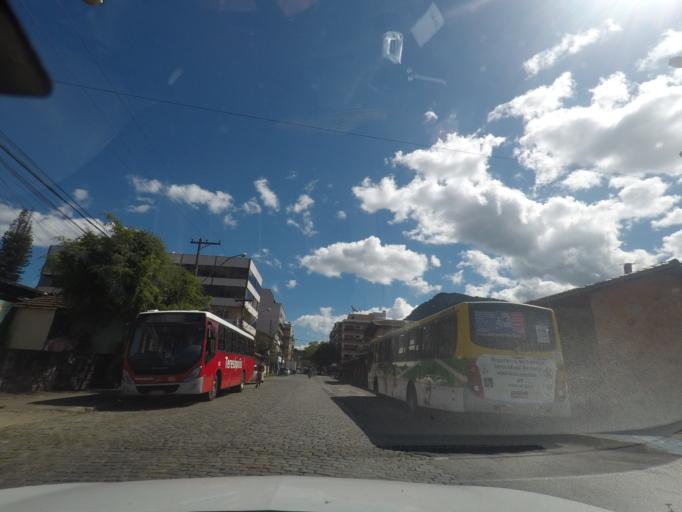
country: BR
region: Rio de Janeiro
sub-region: Teresopolis
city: Teresopolis
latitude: -22.4424
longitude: -42.9784
